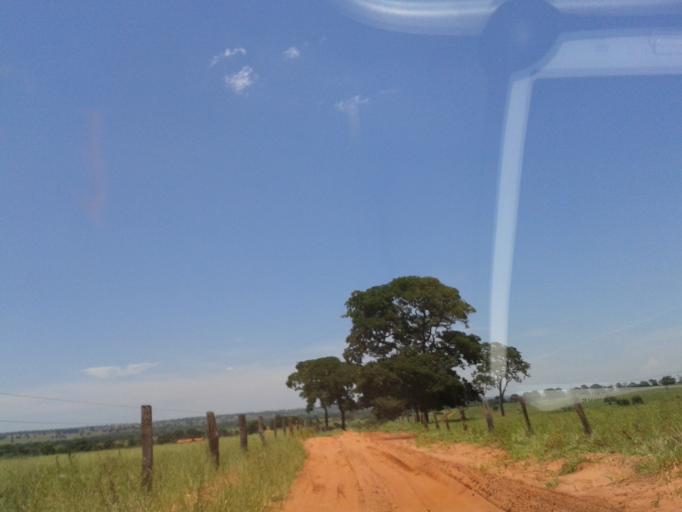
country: BR
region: Minas Gerais
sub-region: Santa Vitoria
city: Santa Vitoria
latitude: -19.2070
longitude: -50.3971
